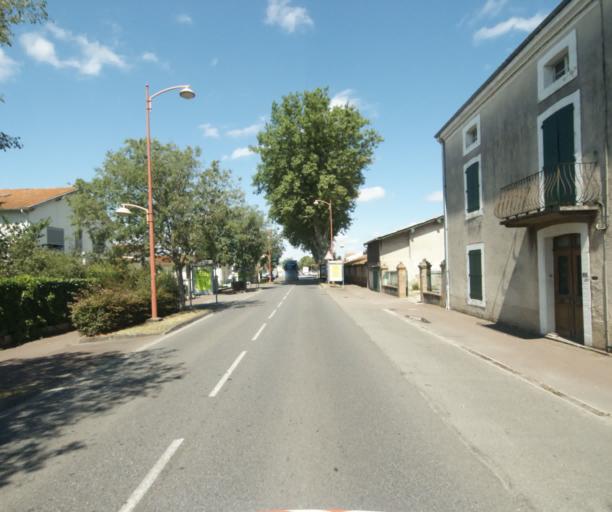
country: FR
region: Midi-Pyrenees
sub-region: Departement de la Haute-Garonne
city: Revel
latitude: 43.4626
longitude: 2.0068
